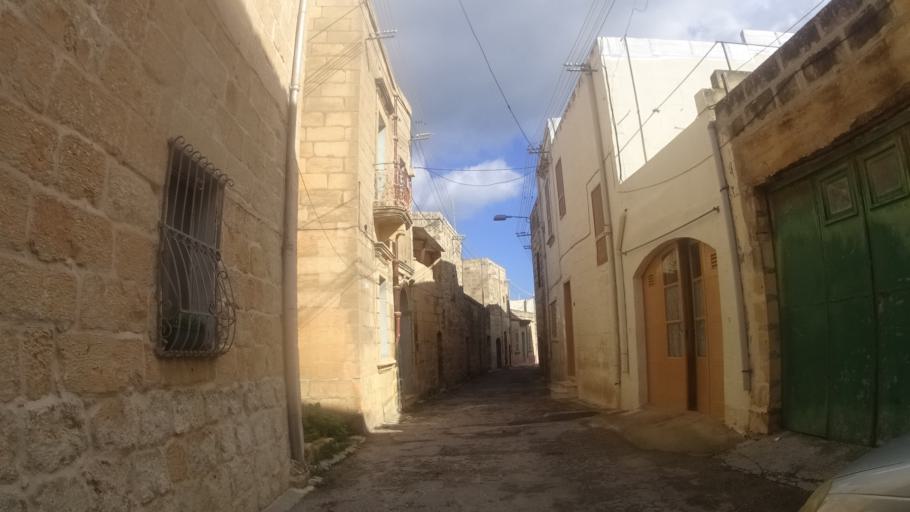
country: MT
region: In-Nadur
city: Nadur
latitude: 36.0406
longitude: 14.2880
